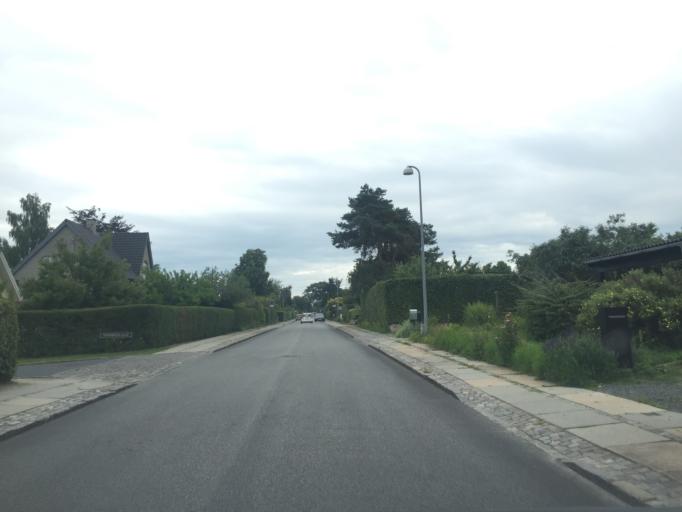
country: DK
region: Capital Region
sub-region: Lyngby-Tarbaek Kommune
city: Kongens Lyngby
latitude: 55.7932
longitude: 12.5418
